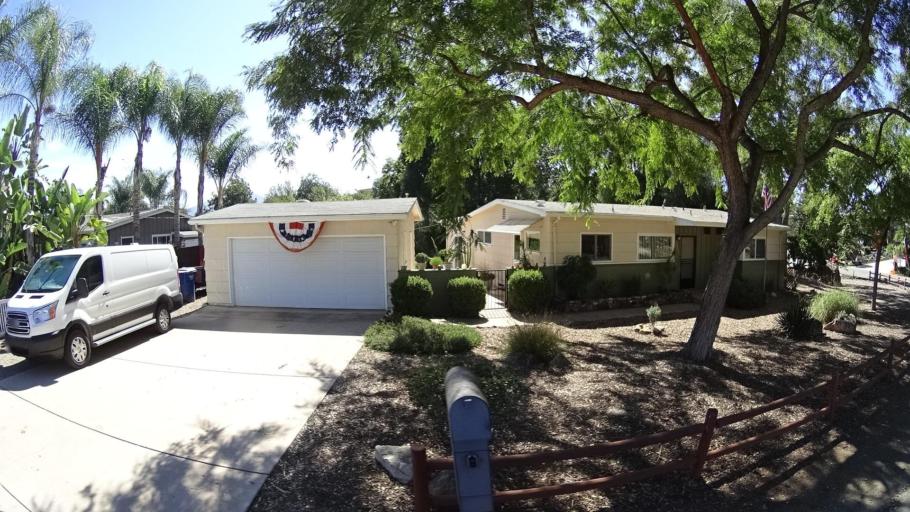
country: US
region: California
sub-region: San Diego County
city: Casa de Oro-Mount Helix
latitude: 32.7546
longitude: -116.9709
